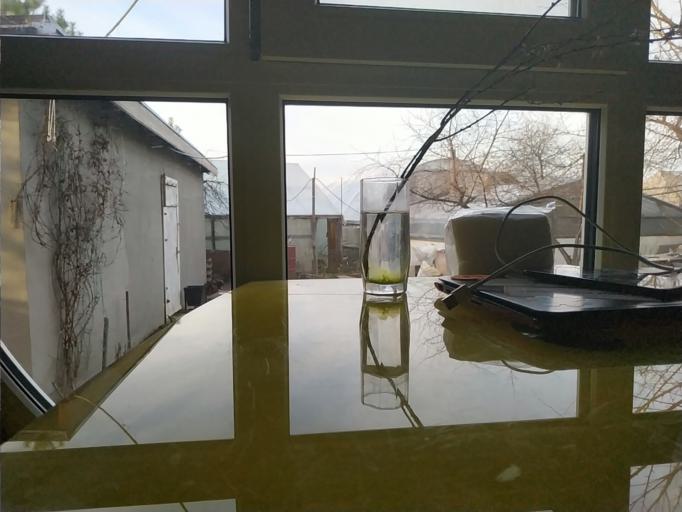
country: RU
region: Republic of Karelia
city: Suoyarvi
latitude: 62.1510
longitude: 32.1406
